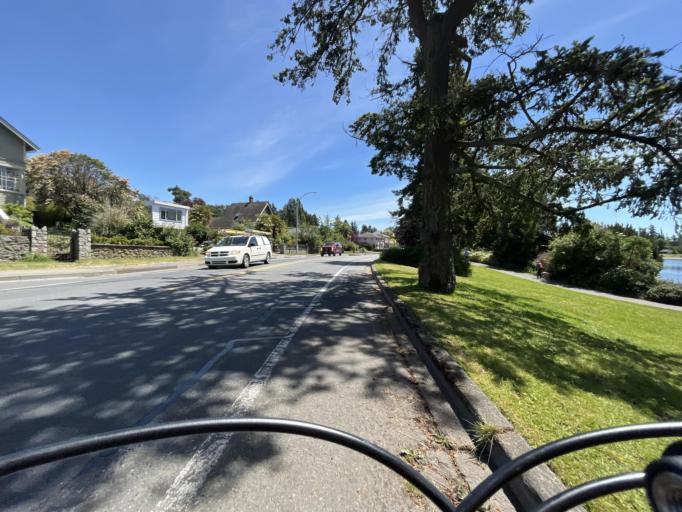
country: CA
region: British Columbia
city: Victoria
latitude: 48.4503
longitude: -123.4098
